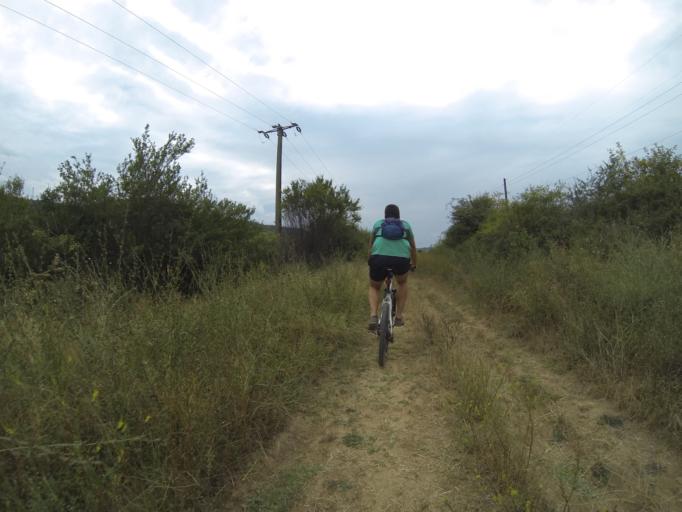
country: RO
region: Dolj
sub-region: Comuna Cotofenii din Fata
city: Cotofenii din Fata
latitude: 44.4837
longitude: 23.6813
